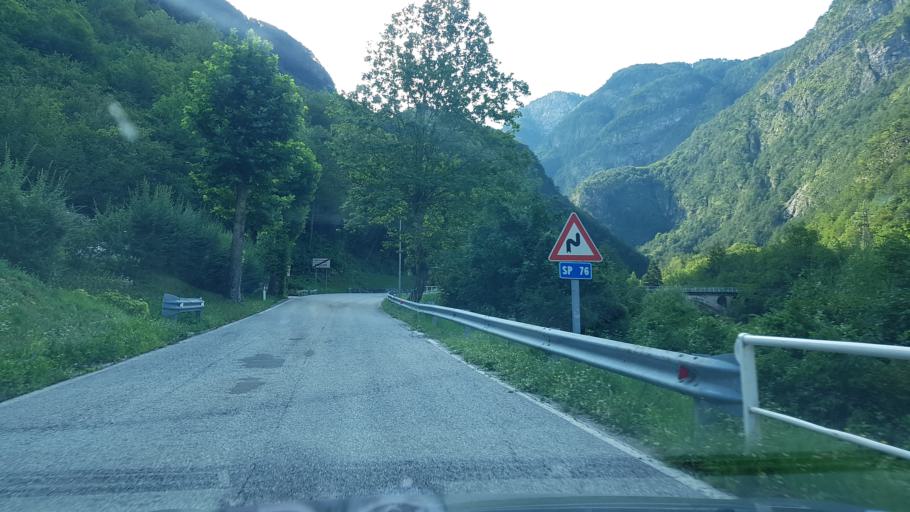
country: IT
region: Friuli Venezia Giulia
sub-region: Provincia di Udine
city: Chiusaforte
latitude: 46.4057
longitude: 13.3164
